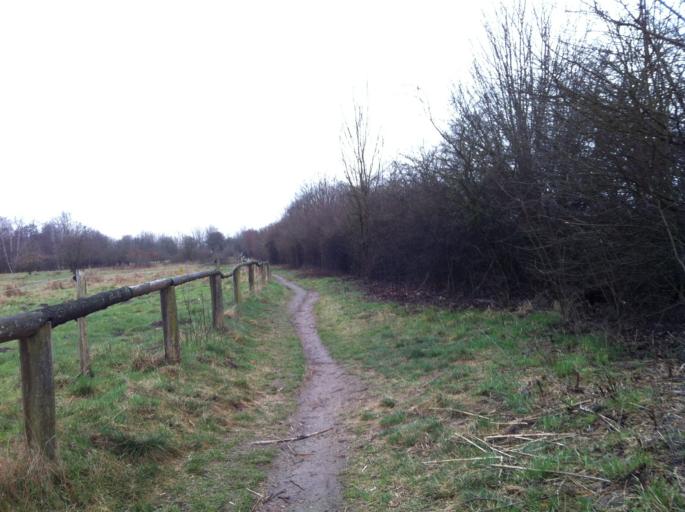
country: DE
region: Berlin
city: Karow
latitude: 52.6260
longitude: 13.4599
